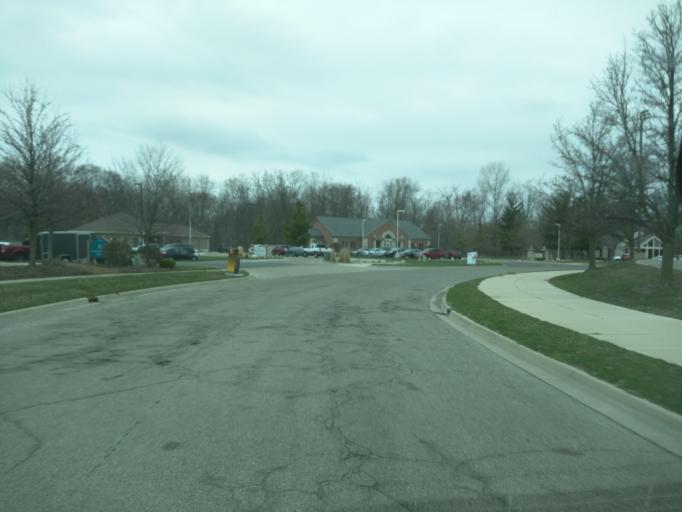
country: US
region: Michigan
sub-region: Ingham County
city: Holt
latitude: 42.6818
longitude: -84.5165
